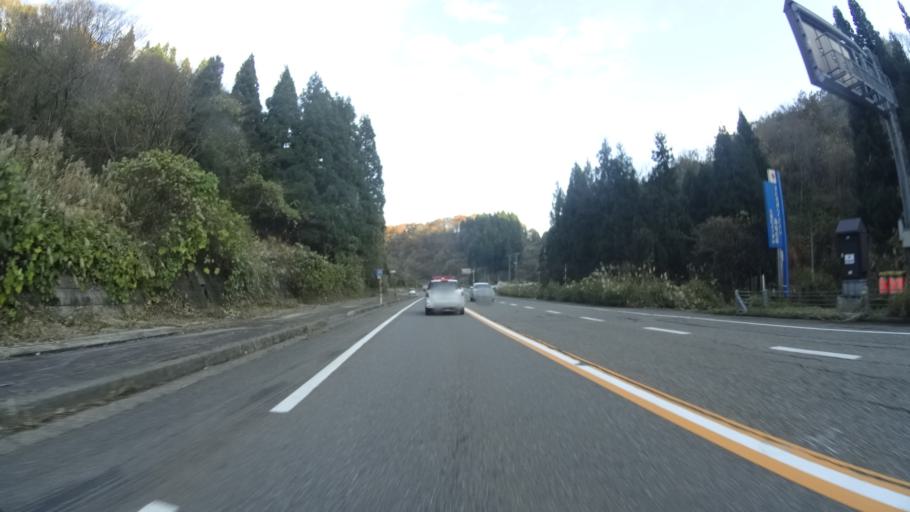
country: JP
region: Niigata
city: Kashiwazaki
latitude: 37.4099
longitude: 138.6679
